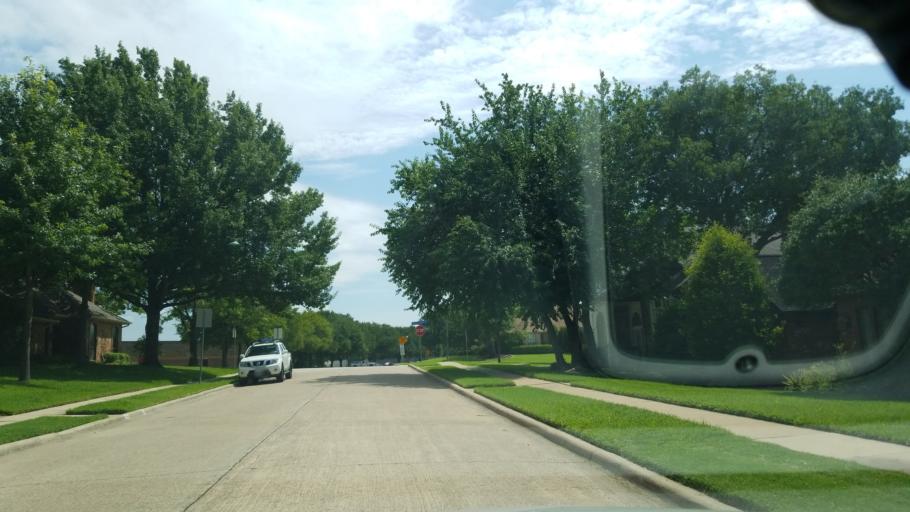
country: US
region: Texas
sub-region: Dallas County
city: Coppell
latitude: 32.9596
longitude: -96.9698
